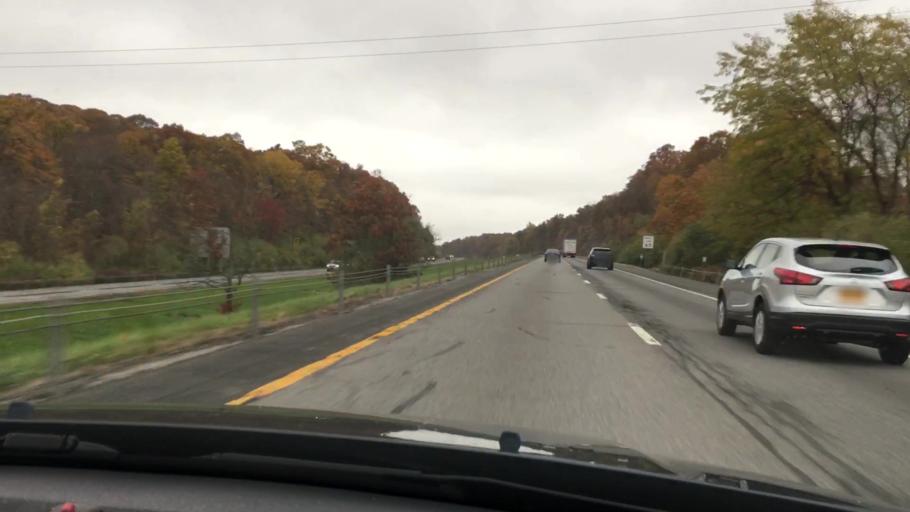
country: US
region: New York
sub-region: Putnam County
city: Brewster Hill
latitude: 41.4359
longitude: -73.6311
